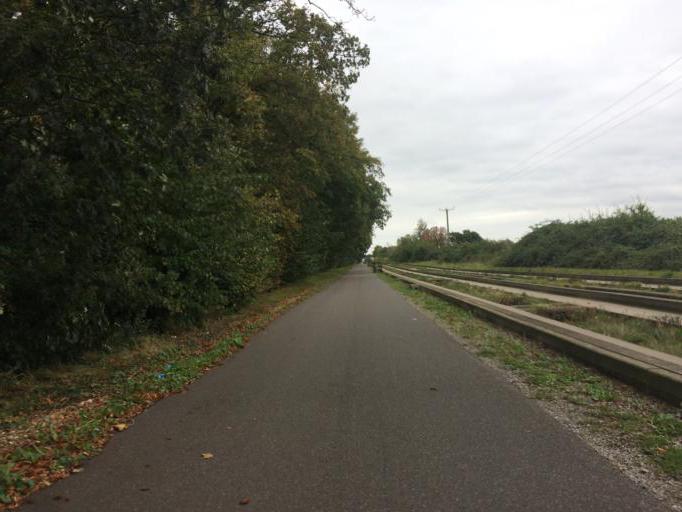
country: GB
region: England
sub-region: Cambridgeshire
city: Histon
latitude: 52.2395
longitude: 0.1189
